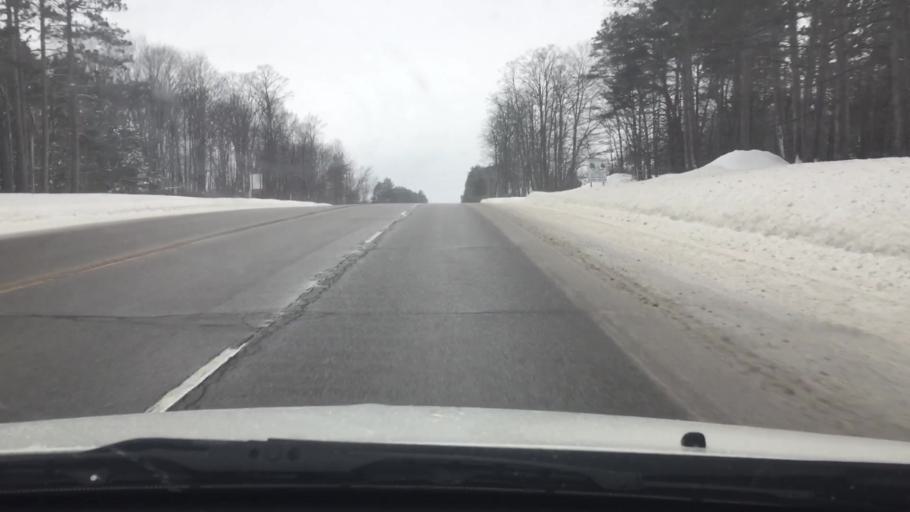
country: US
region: Michigan
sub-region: Otsego County
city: Gaylord
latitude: 45.0621
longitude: -84.8256
